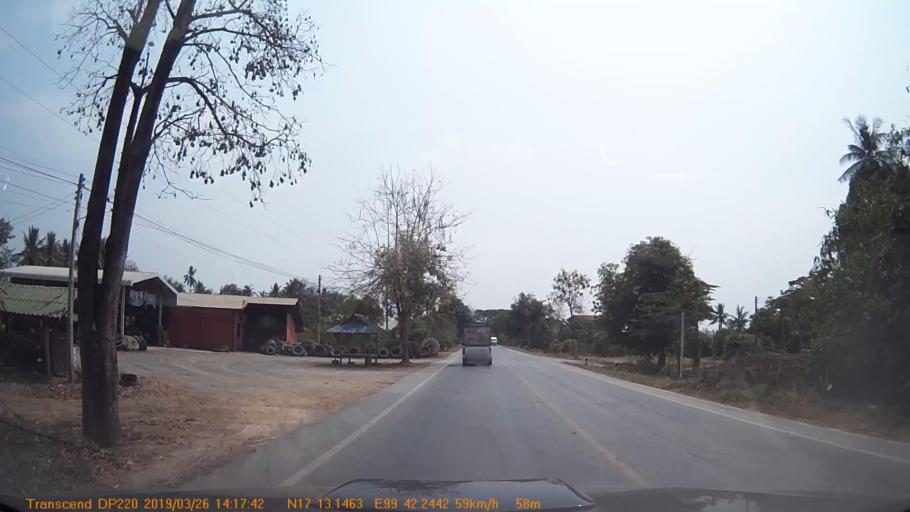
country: TH
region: Sukhothai
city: Sawankhalok
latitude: 17.2188
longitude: 99.7039
